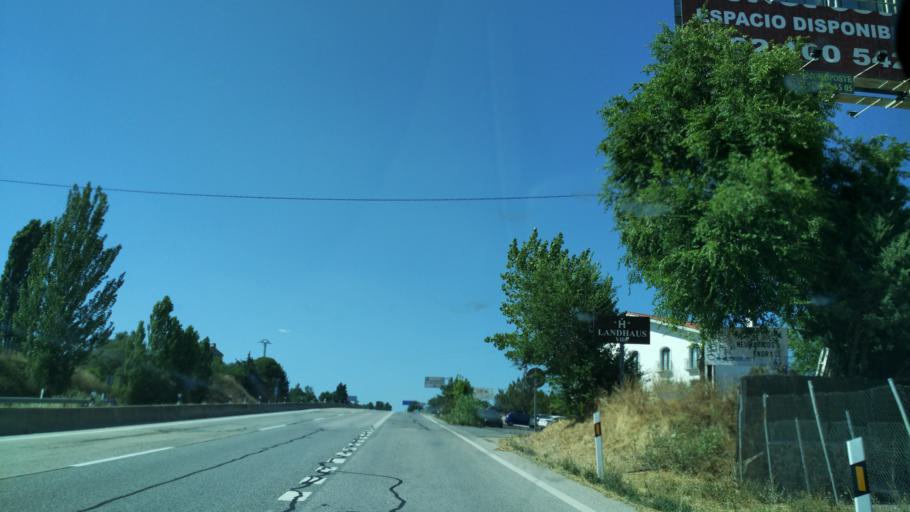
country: ES
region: Madrid
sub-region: Provincia de Madrid
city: El Molar
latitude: 40.7354
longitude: -3.5859
